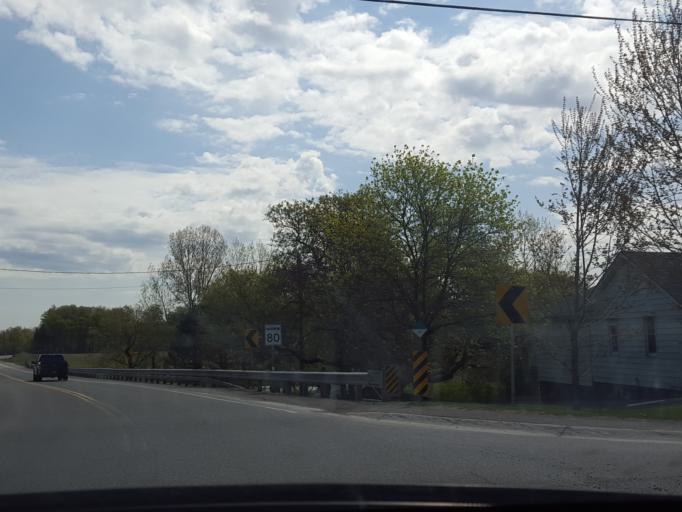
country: CA
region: Ontario
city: Oshawa
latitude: 44.1185
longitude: -78.8282
